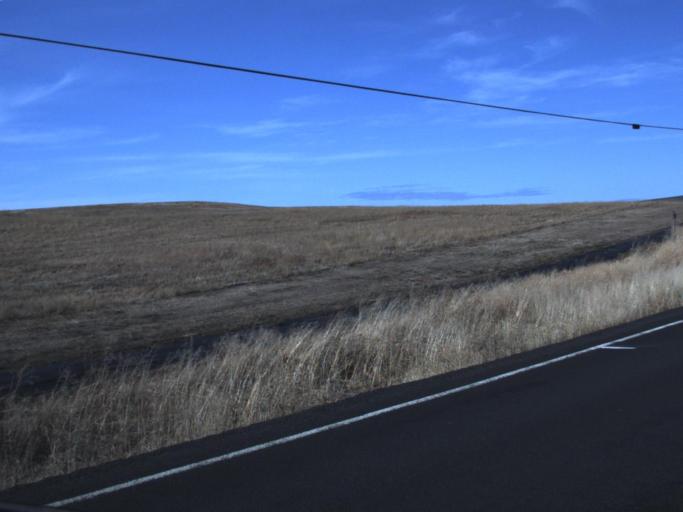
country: US
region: Washington
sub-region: Lincoln County
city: Davenport
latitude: 47.6733
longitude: -118.1410
